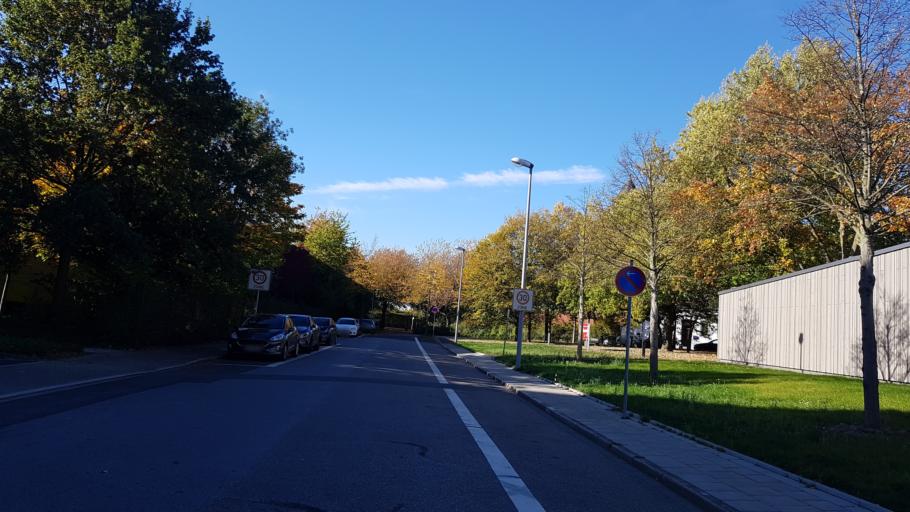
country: DE
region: North Rhine-Westphalia
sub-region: Regierungsbezirk Dusseldorf
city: Muelheim (Ruhr)
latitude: 51.4435
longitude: 6.8595
